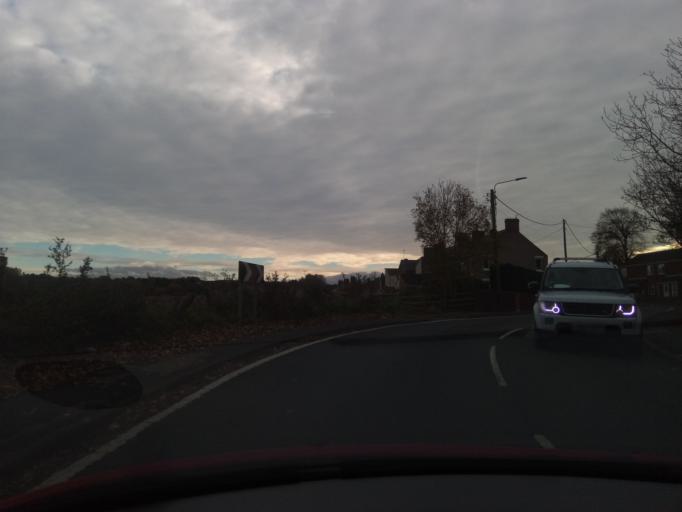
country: GB
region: England
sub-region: County Durham
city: Bishop Auckland
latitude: 54.6489
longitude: -1.6606
